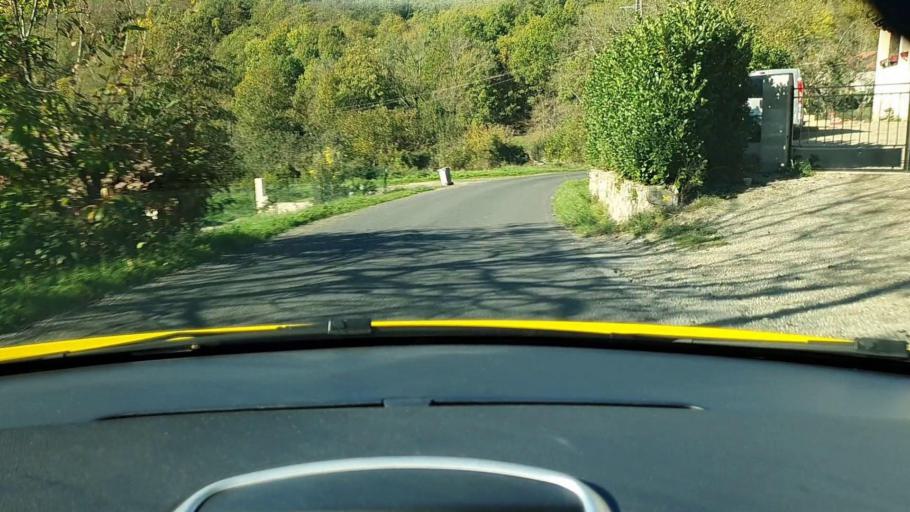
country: FR
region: Languedoc-Roussillon
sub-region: Departement du Gard
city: Le Vigan
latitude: 43.9875
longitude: 3.4987
